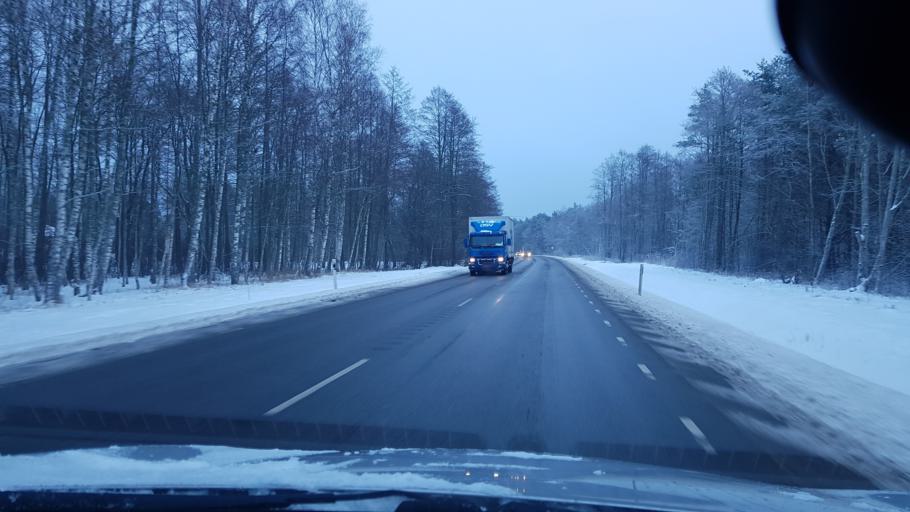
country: EE
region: Harju
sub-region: Paldiski linn
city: Paldiski
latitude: 59.3369
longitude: 24.2334
